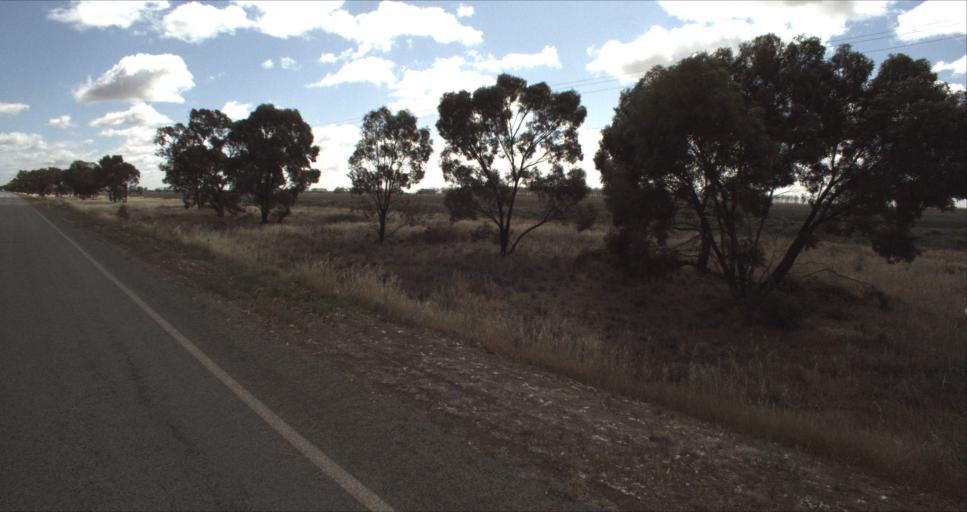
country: AU
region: New South Wales
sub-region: Murrumbidgee Shire
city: Darlington Point
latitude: -34.5680
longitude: 146.1677
